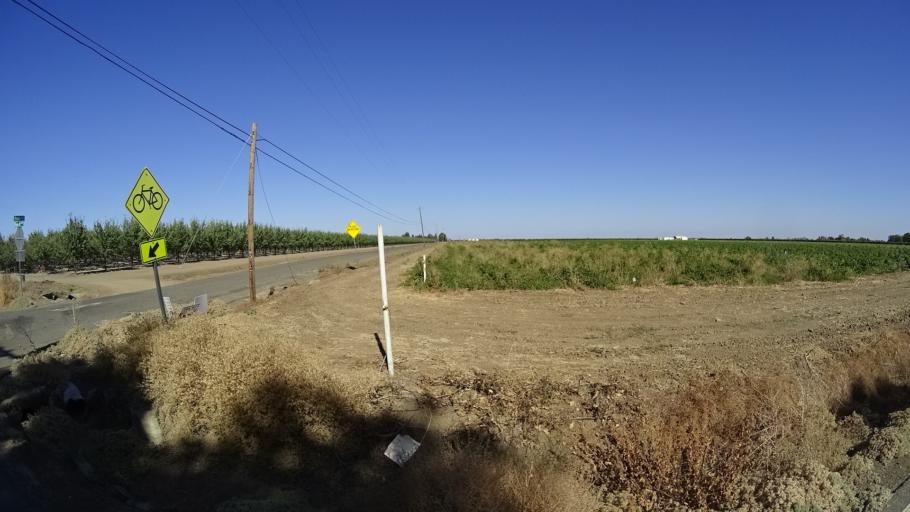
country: US
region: California
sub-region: Yolo County
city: Davis
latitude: 38.5470
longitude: -121.8215
